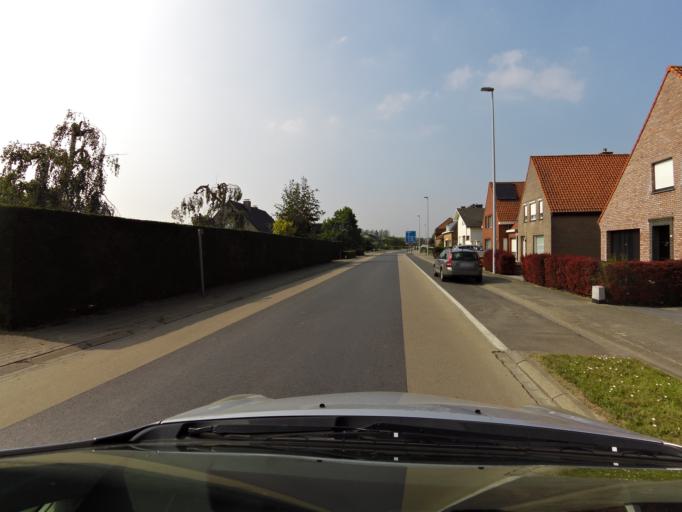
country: BE
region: Flanders
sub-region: Provincie West-Vlaanderen
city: Poperinge
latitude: 50.8622
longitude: 2.7188
